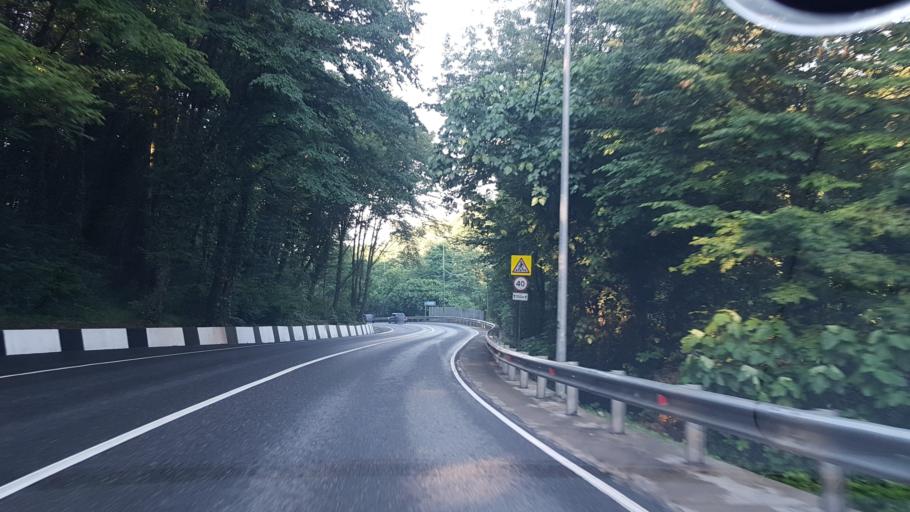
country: RU
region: Krasnodarskiy
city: Gornoye Loo
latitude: 43.6714
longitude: 39.6206
